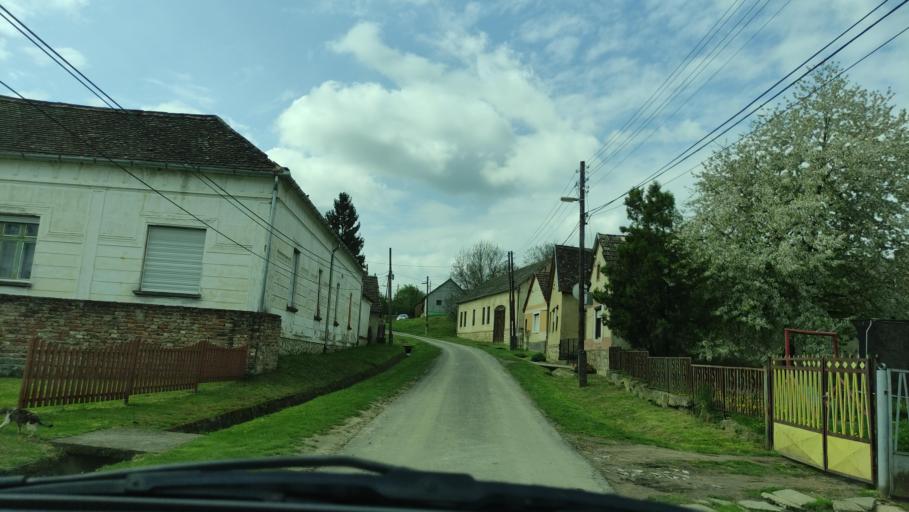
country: HU
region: Baranya
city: Sasd
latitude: 46.2854
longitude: 18.1716
